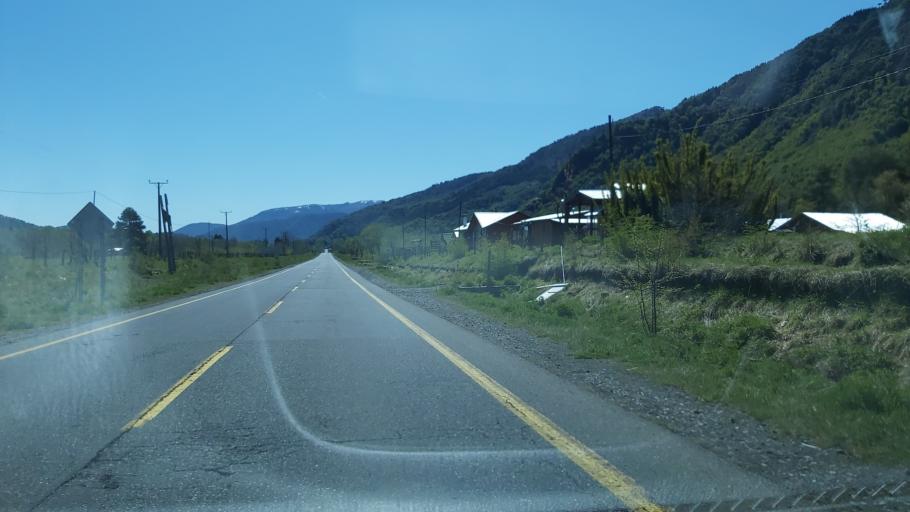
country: CL
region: Araucania
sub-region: Provincia de Cautin
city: Vilcun
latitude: -38.4774
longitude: -71.5411
